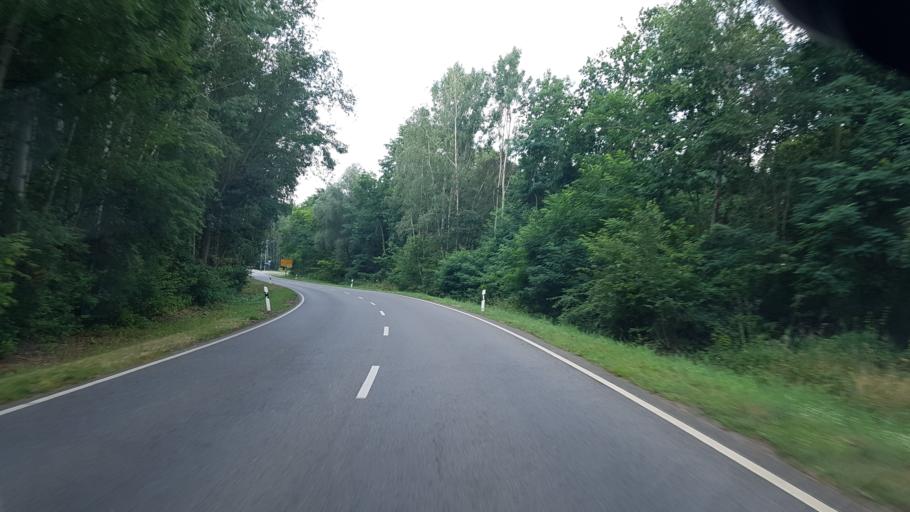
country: DE
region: Brandenburg
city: Lauchhammer
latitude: 51.4970
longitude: 13.7385
